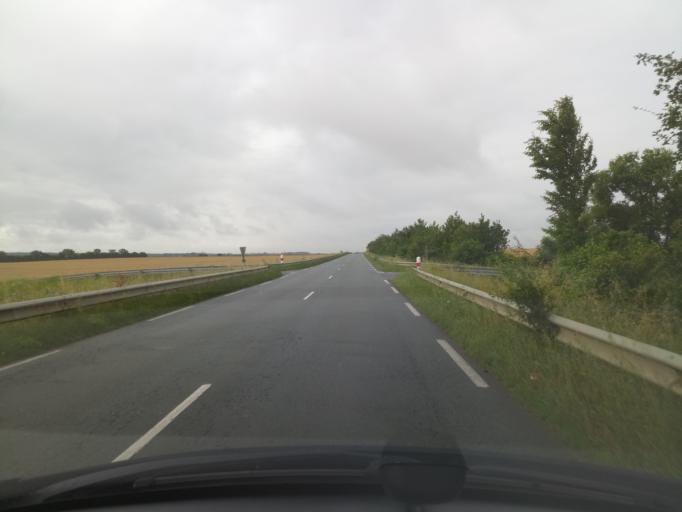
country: FR
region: Poitou-Charentes
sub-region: Departement de la Charente-Maritime
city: Saint-Jean-de-Liversay
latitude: 46.2063
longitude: -0.8740
